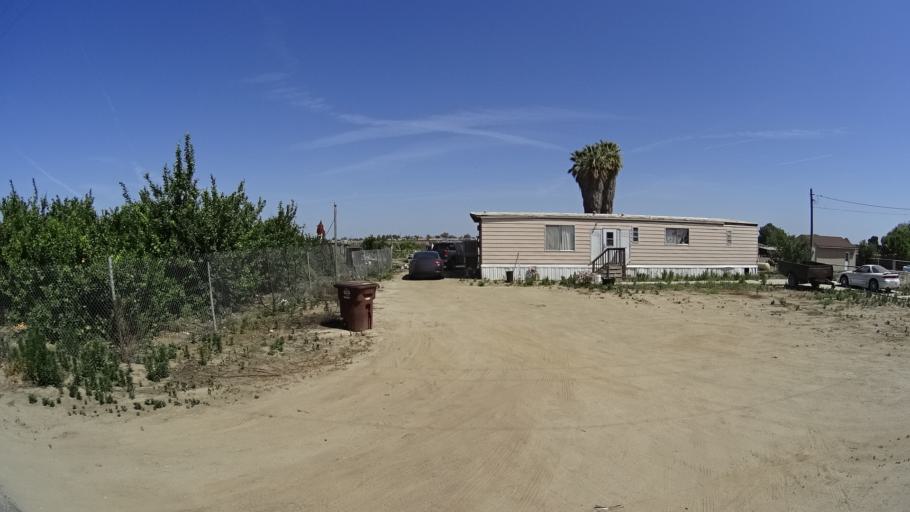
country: US
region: California
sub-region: Kings County
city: Lemoore
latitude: 36.2692
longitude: -119.7879
